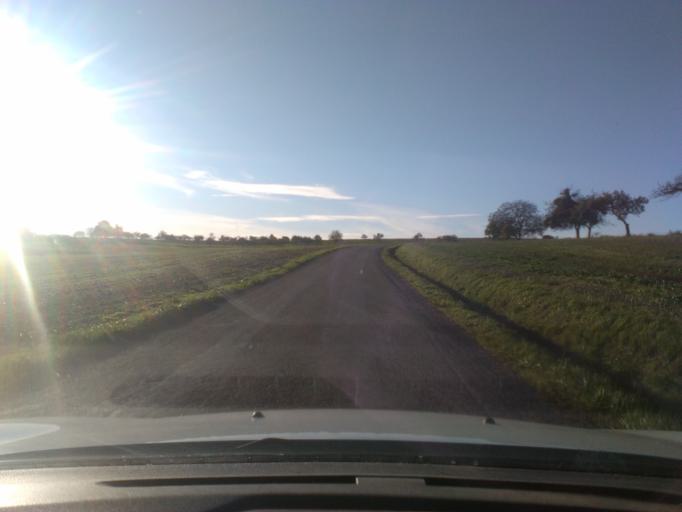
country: FR
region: Lorraine
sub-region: Departement des Vosges
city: Chatel-sur-Moselle
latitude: 48.3232
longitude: 6.4529
